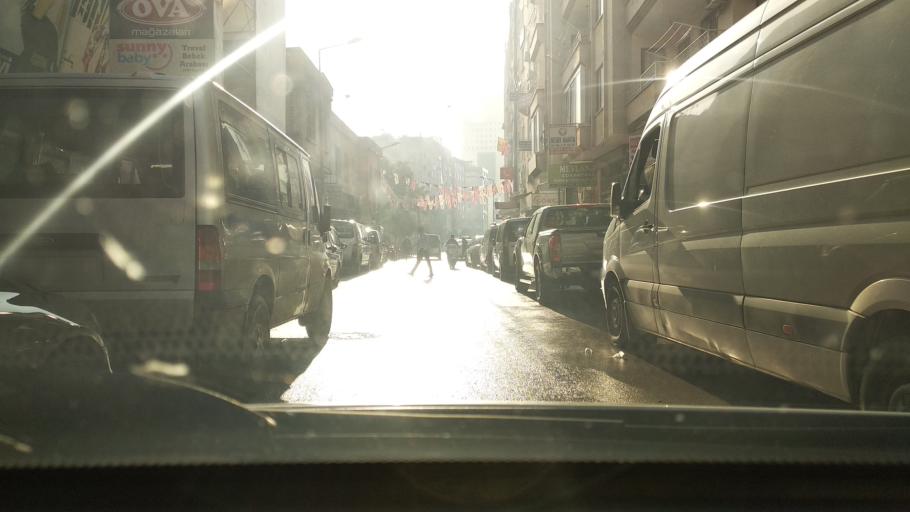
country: TR
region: Mersin
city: Mercin
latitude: 36.8058
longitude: 34.6224
